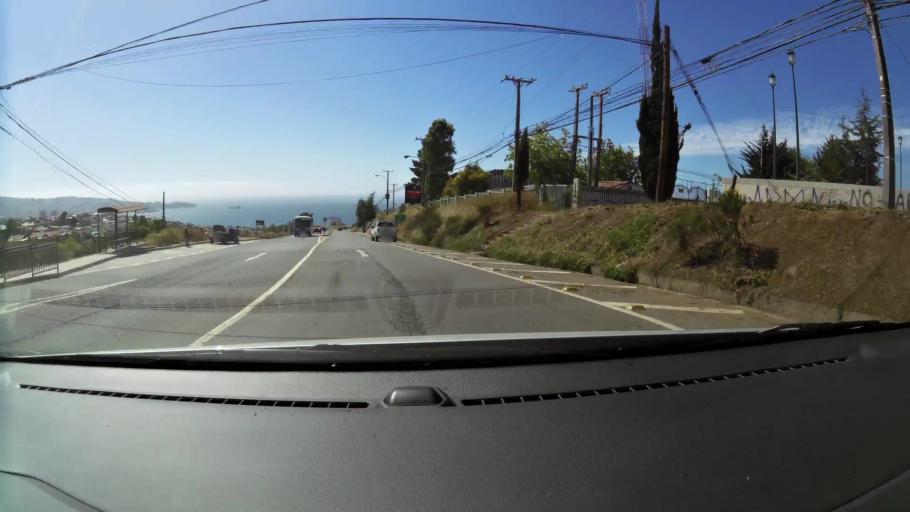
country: CL
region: Valparaiso
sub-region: Provincia de Valparaiso
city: Vina del Mar
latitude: -33.0402
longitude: -71.5693
